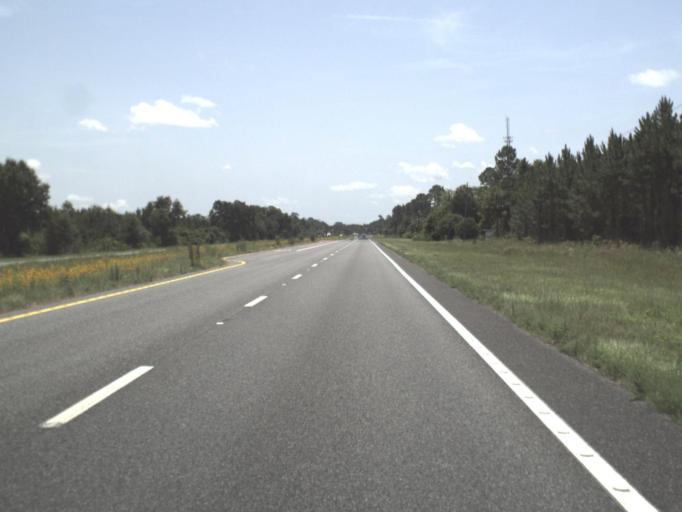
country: US
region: Florida
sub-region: Taylor County
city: Steinhatchee
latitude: 29.7854
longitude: -83.3304
